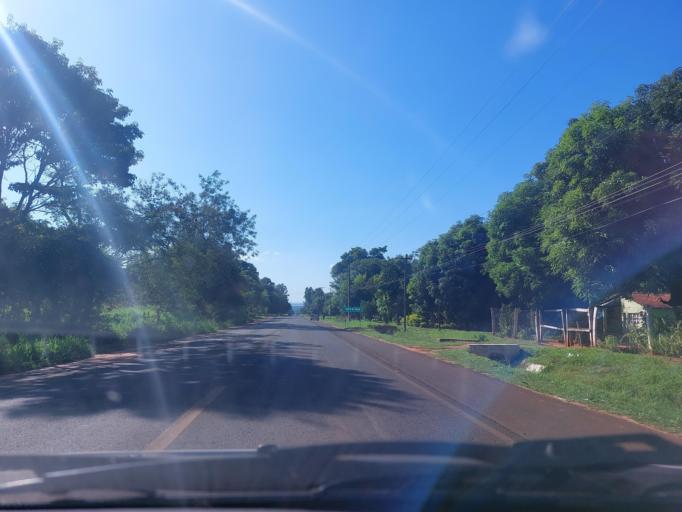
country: PY
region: San Pedro
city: Guayaybi
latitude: -24.5314
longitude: -56.4352
